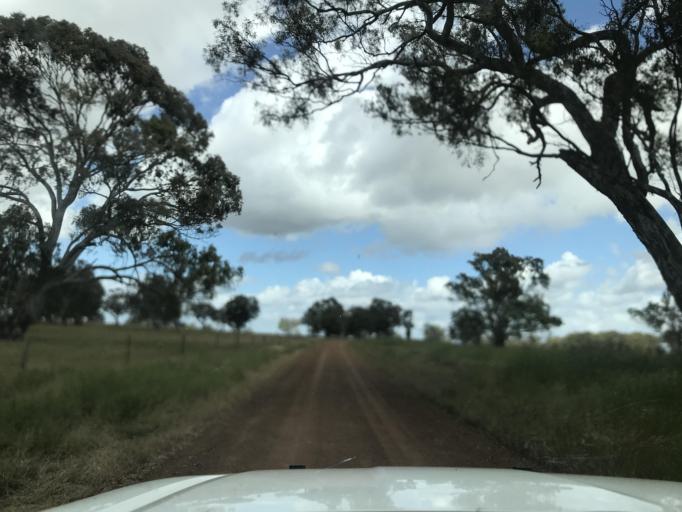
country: AU
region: South Australia
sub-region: Wattle Range
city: Penola
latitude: -37.1944
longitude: 141.4268
